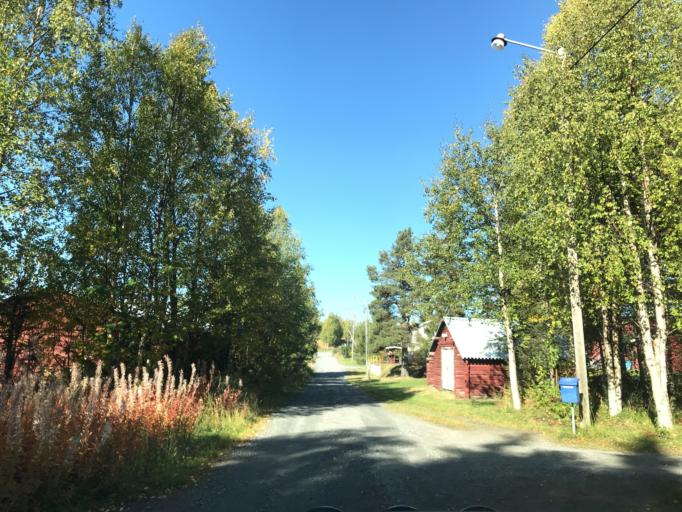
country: SE
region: Norrbotten
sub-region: Gallivare Kommun
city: Malmberget
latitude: 67.6453
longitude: 21.0667
